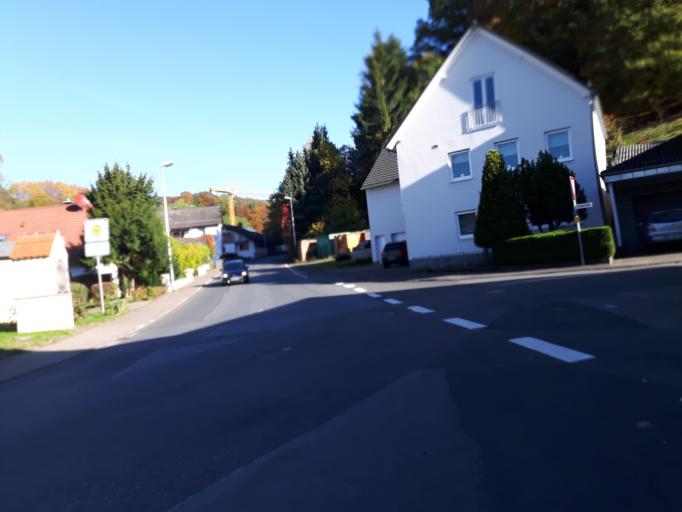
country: DE
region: Bavaria
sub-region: Regierungsbezirk Unterfranken
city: Leidersbach
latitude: 49.8943
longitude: 9.2356
